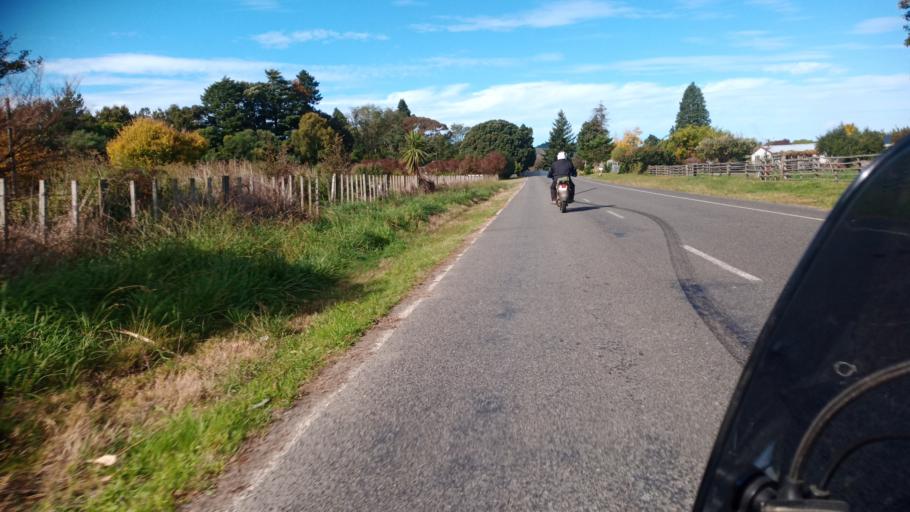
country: NZ
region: Hawke's Bay
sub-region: Wairoa District
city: Wairoa
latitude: -39.0712
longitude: 177.1453
